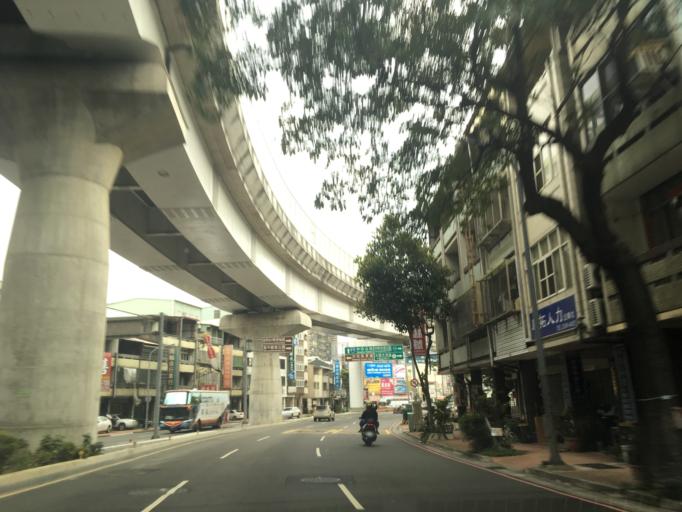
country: TW
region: Taiwan
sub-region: Taichung City
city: Taichung
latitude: 24.1719
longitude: 120.6983
